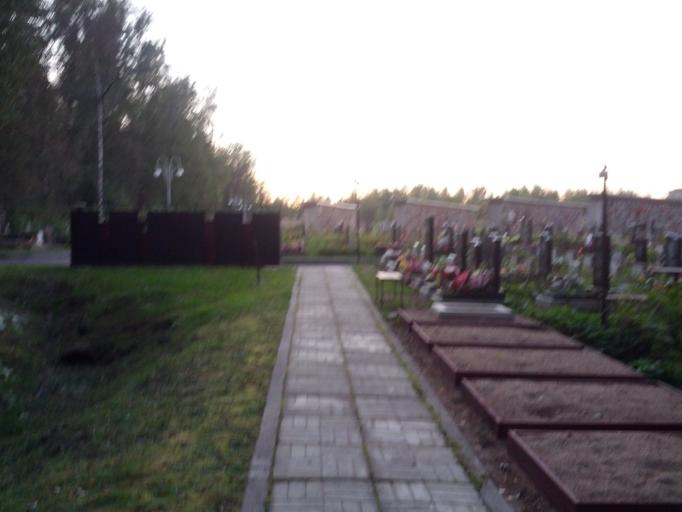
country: RU
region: St.-Petersburg
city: Obukhovo
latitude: 59.9122
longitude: 30.4322
